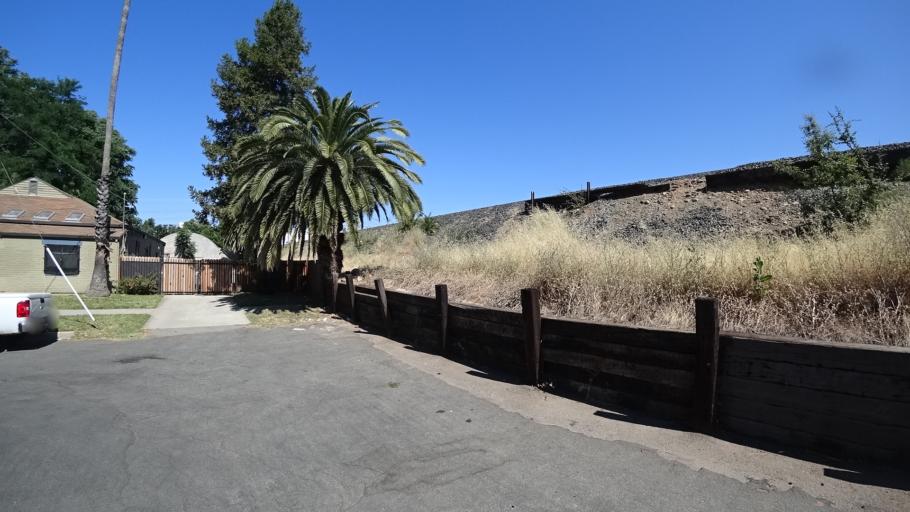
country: US
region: California
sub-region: Sacramento County
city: Sacramento
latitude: 38.5849
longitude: -121.4749
